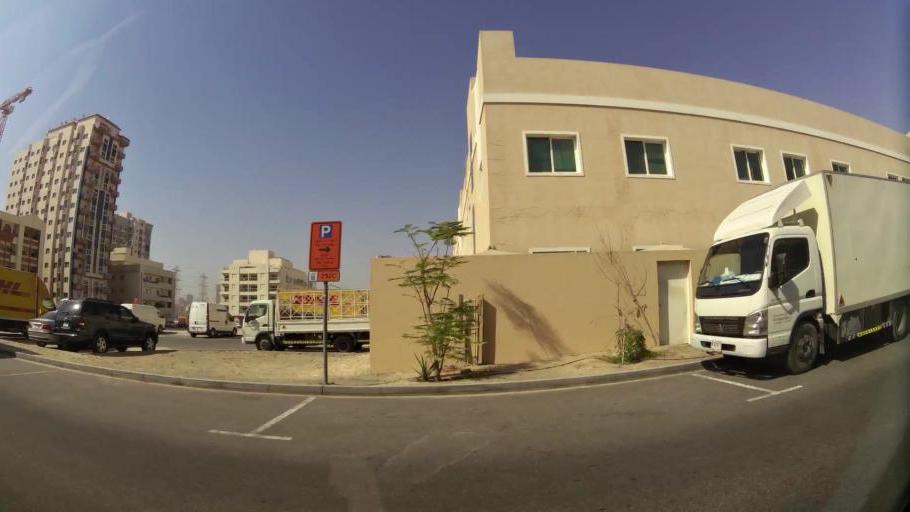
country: AE
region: Ash Shariqah
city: Sharjah
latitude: 25.2785
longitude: 55.3743
